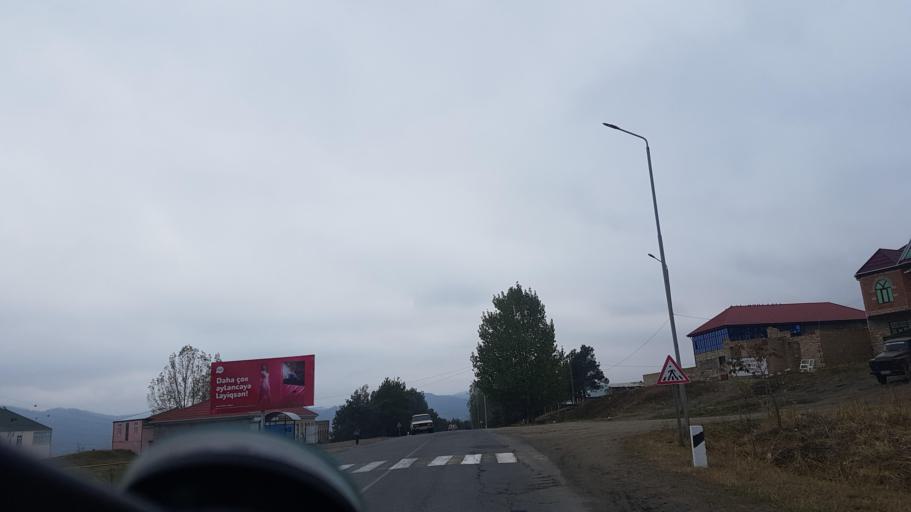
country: AZ
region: Gadabay Rayon
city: Ariqdam
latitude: 40.6072
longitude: 45.8125
